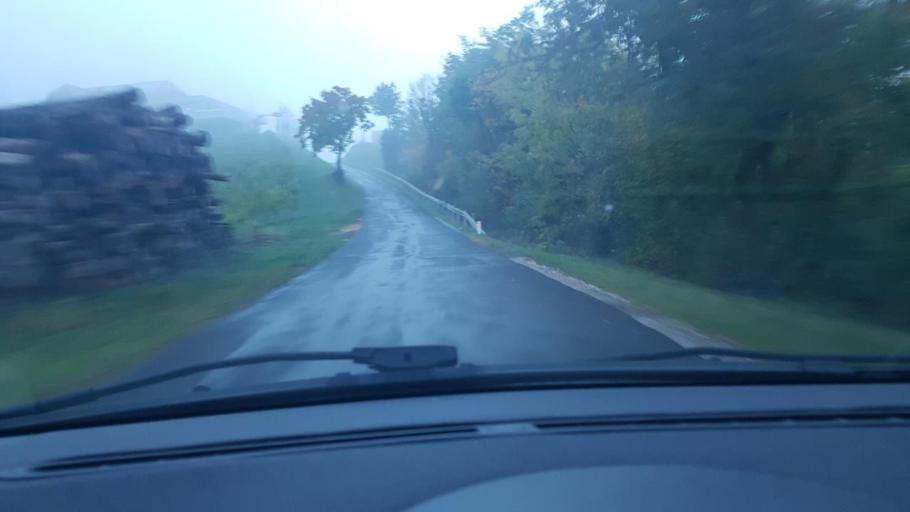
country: AT
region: Styria
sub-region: Politischer Bezirk Leibnitz
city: Sulztal an der Weinstrasse
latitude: 46.6717
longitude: 15.5366
